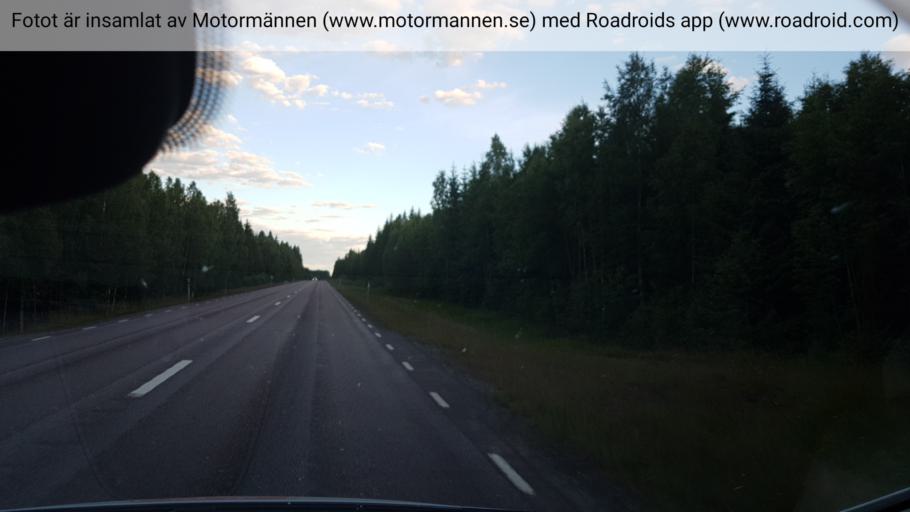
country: SE
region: Vaermland
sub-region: Torsby Kommun
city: Torsby
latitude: 60.0625
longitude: 13.0548
